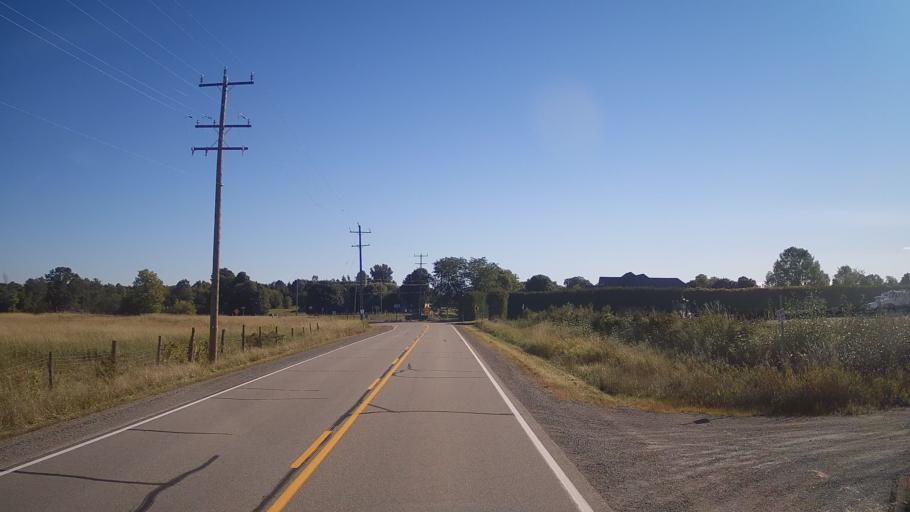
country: CA
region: Ontario
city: Gananoque
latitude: 44.5944
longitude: -76.0911
